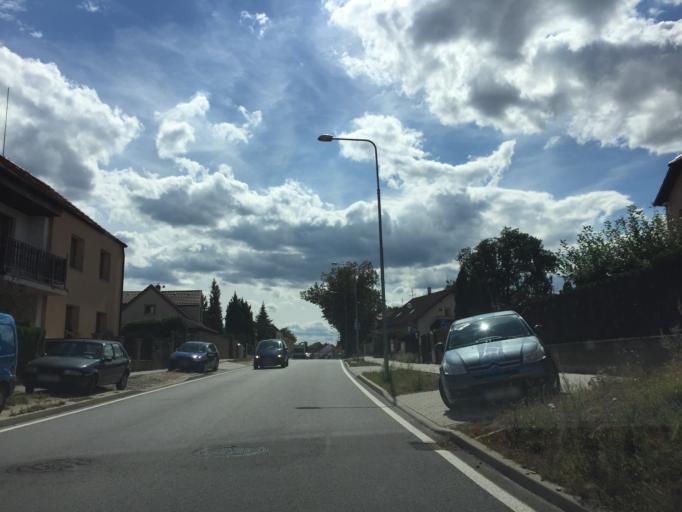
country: CZ
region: Jihocesky
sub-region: Okres Ceske Budejovice
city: Ceske Budejovice
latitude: 48.9453
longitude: 14.4820
